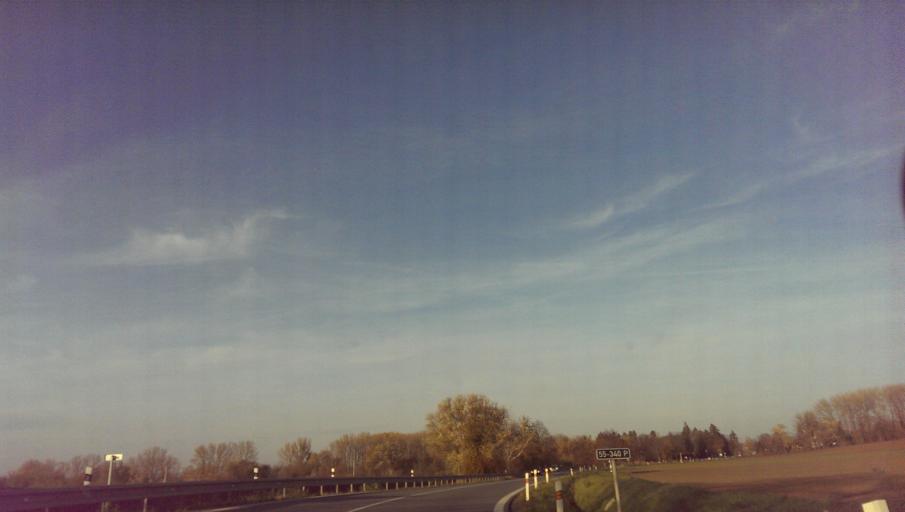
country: CZ
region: Zlin
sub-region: Okres Zlin
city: Ostrozska Nova Ves
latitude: 49.0131
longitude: 17.4419
